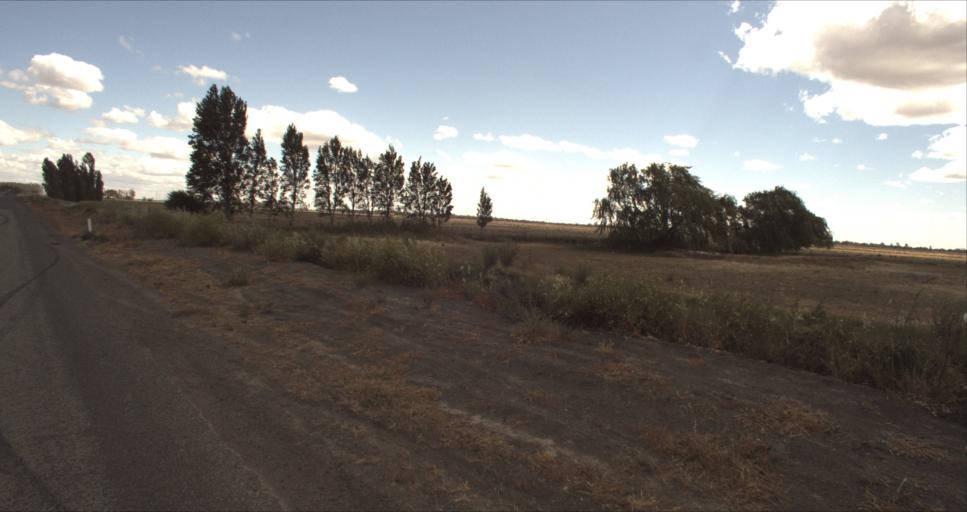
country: AU
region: New South Wales
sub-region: Leeton
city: Leeton
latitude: -34.5257
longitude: 146.2212
